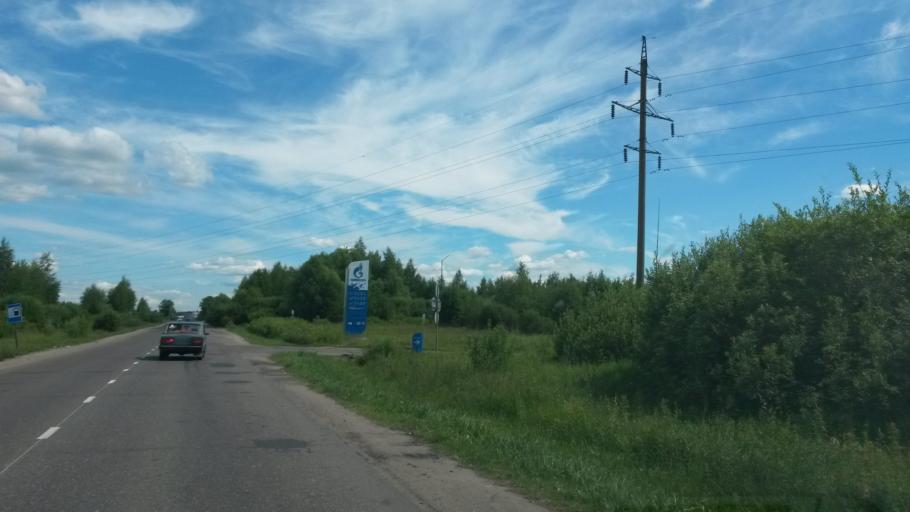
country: RU
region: Ivanovo
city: Zavolzhsk
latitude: 57.5008
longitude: 42.1171
